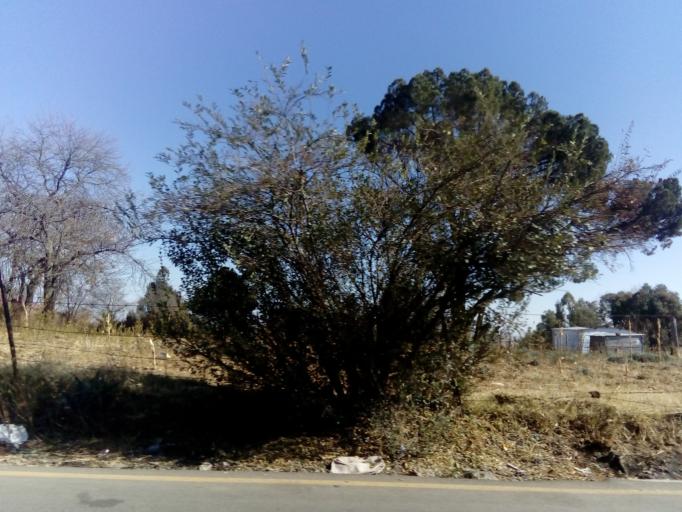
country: LS
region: Berea
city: Teyateyaneng
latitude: -29.1157
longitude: 27.8239
